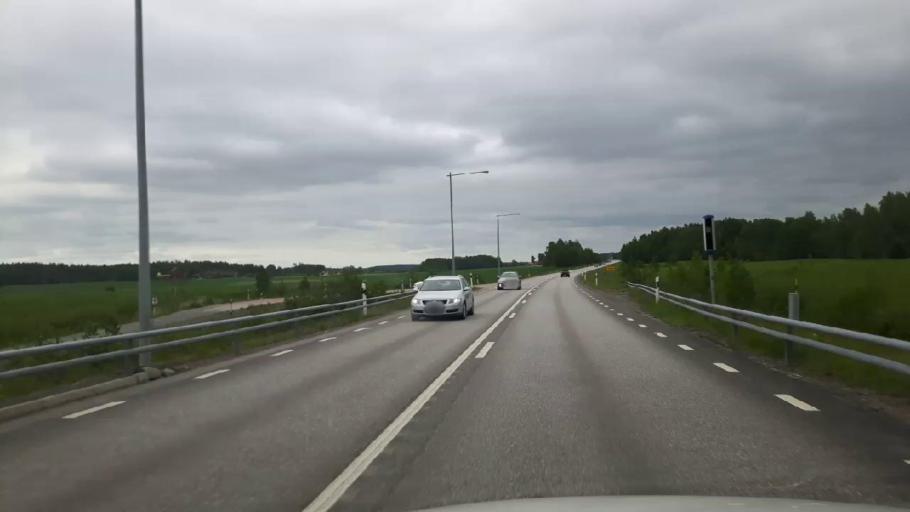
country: SE
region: Vaestmanland
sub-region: Kopings Kommun
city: Koping
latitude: 59.5496
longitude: 15.9164
